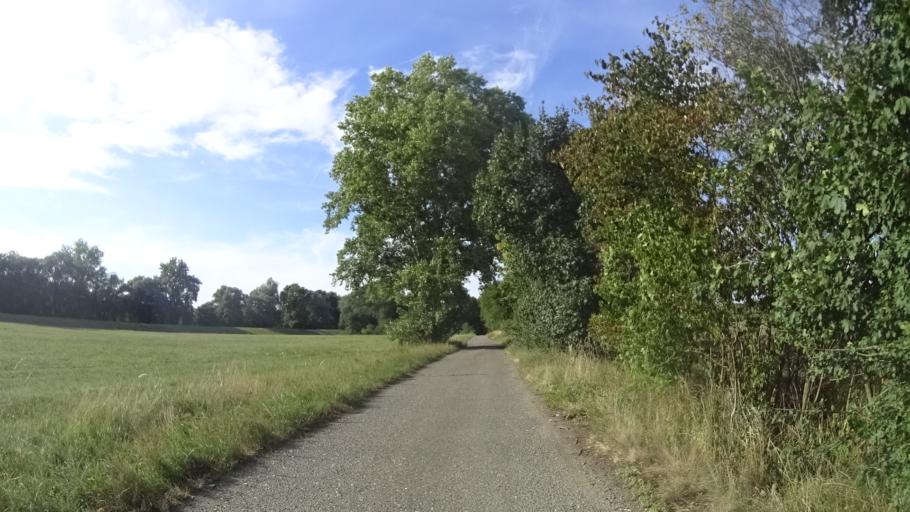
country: AT
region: Lower Austria
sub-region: Politischer Bezirk Mistelbach
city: Rabensburg
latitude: 48.6058
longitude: 16.9483
